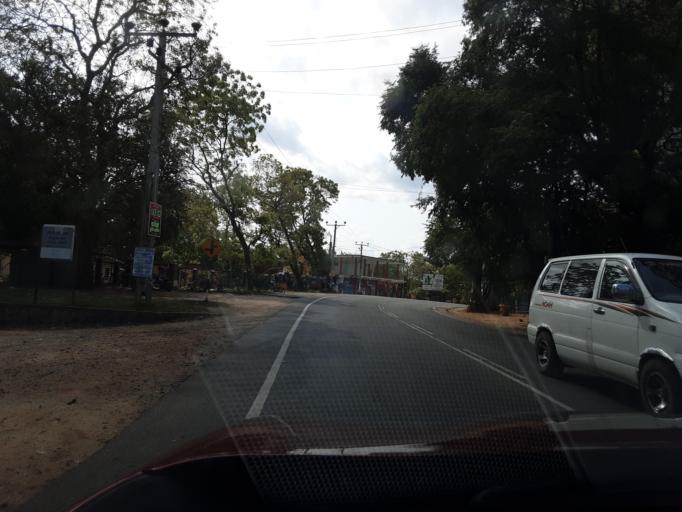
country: LK
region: Uva
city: Haputale
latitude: 6.3466
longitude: 81.1972
